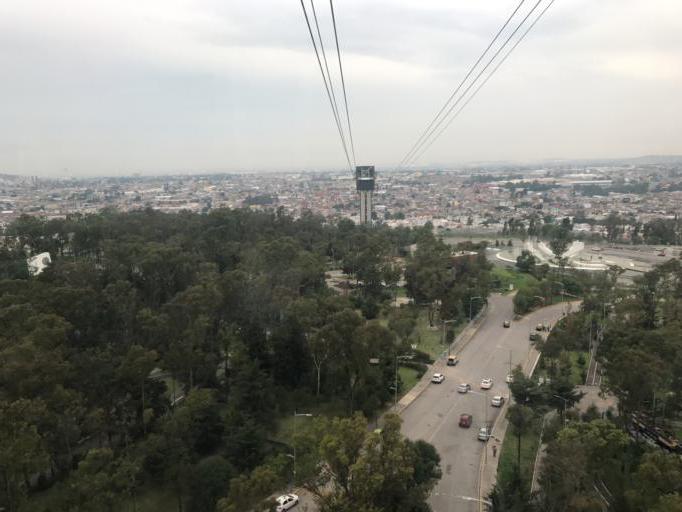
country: MX
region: Puebla
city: Puebla
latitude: 19.0582
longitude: -98.1826
